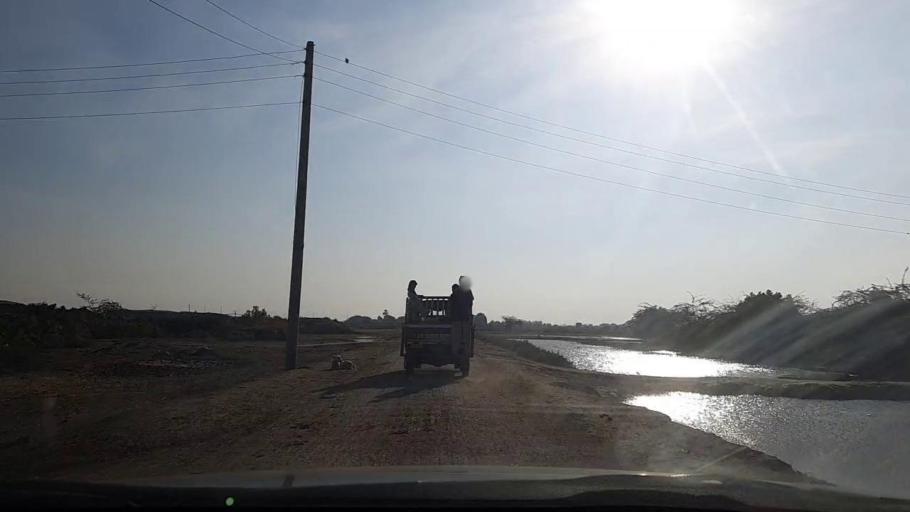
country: PK
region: Sindh
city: Mirpur Sakro
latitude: 24.5294
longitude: 67.6328
